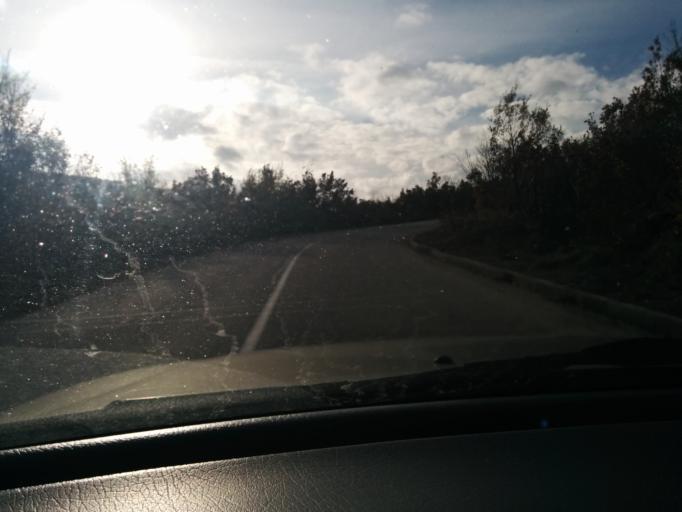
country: HR
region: Splitsko-Dalmatinska
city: Hrvace
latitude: 43.7550
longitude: 16.5764
